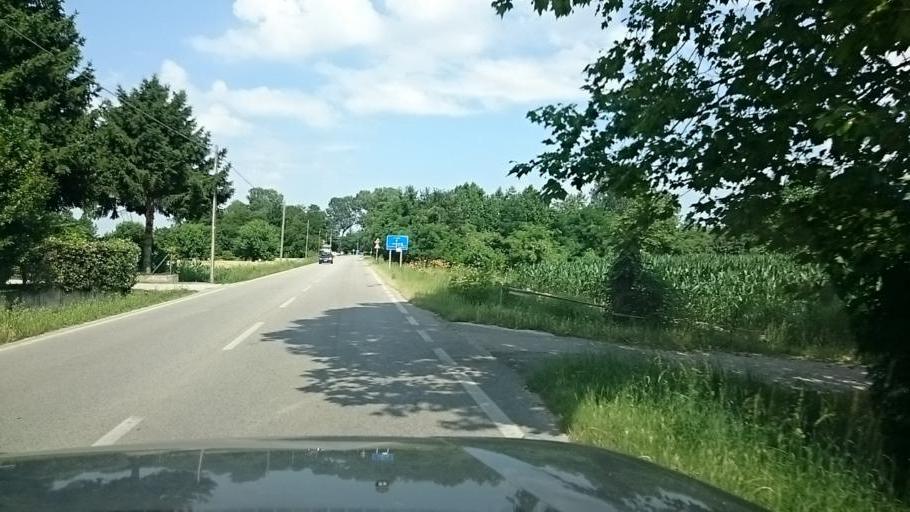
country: IT
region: Veneto
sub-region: Provincia di Vicenza
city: Cartigliano
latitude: 45.7184
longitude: 11.7167
